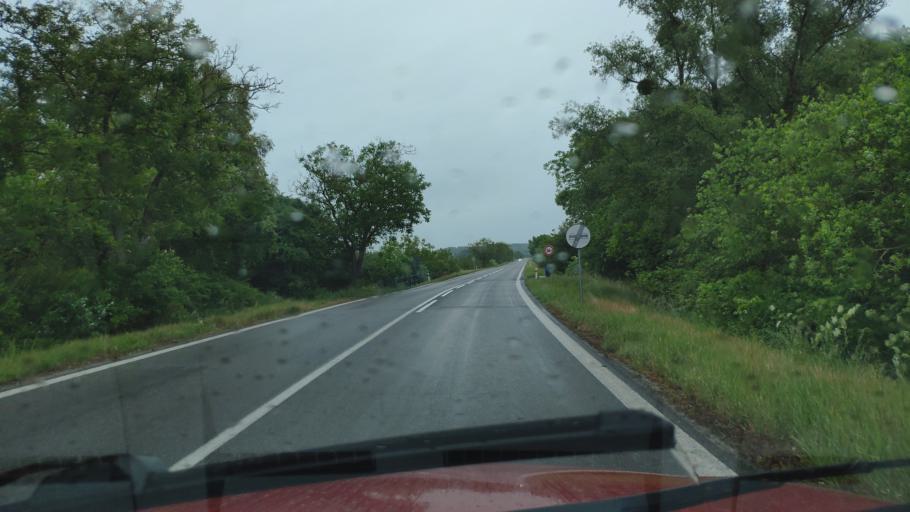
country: HU
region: Borsod-Abauj-Zemplen
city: Ricse
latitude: 48.4335
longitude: 21.8892
